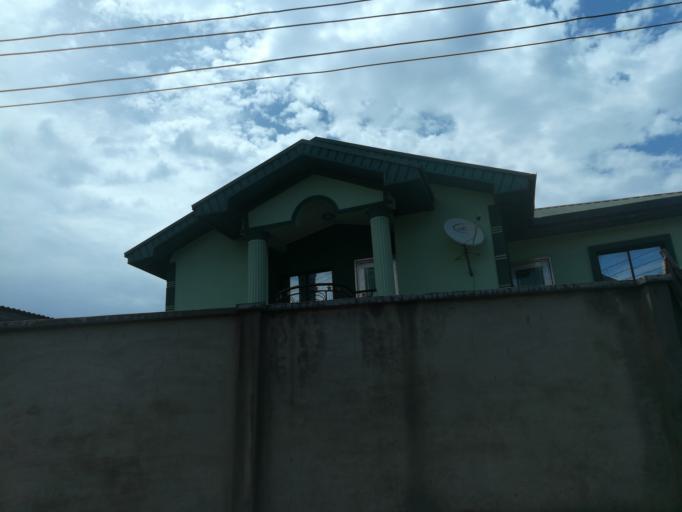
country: NG
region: Lagos
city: Agege
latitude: 6.6056
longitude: 3.3260
